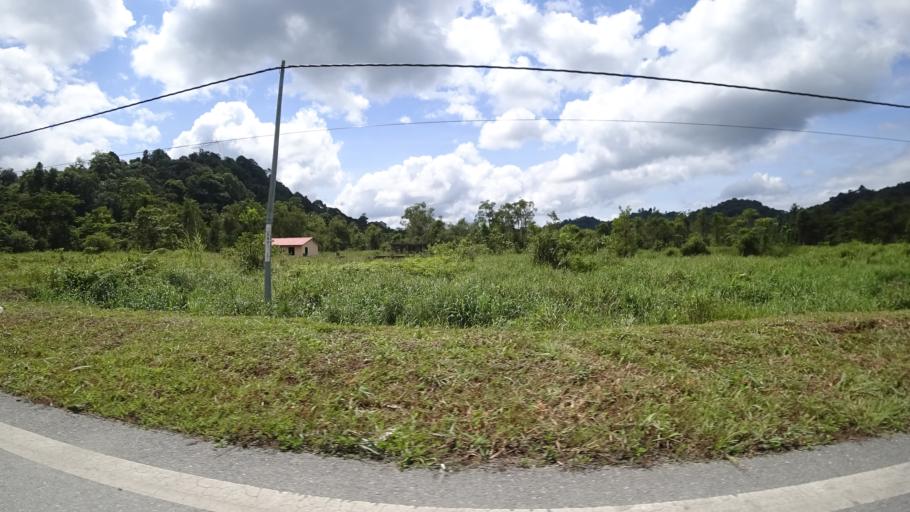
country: MY
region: Sarawak
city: Limbang
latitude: 4.6625
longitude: 114.9442
